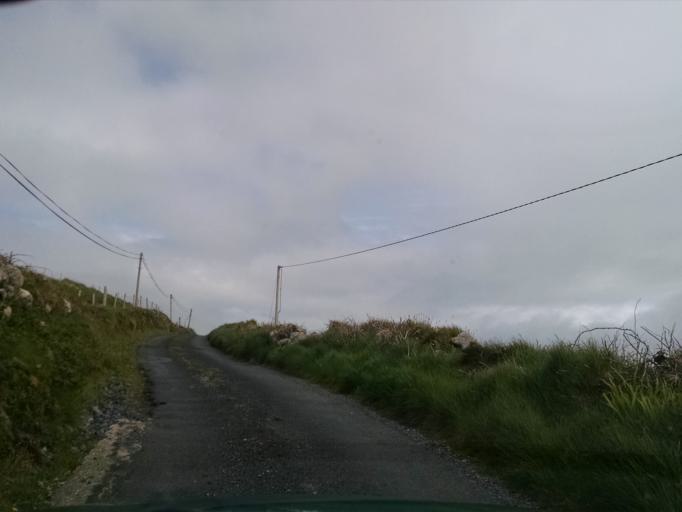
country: IE
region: Connaught
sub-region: County Galway
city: Clifden
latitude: 53.7639
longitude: -9.8760
